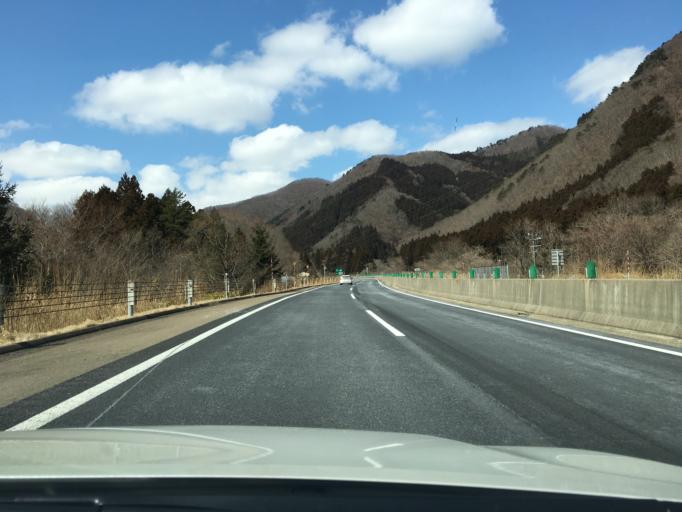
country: JP
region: Yamagata
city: Yamagata-shi
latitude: 38.2077
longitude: 140.5666
